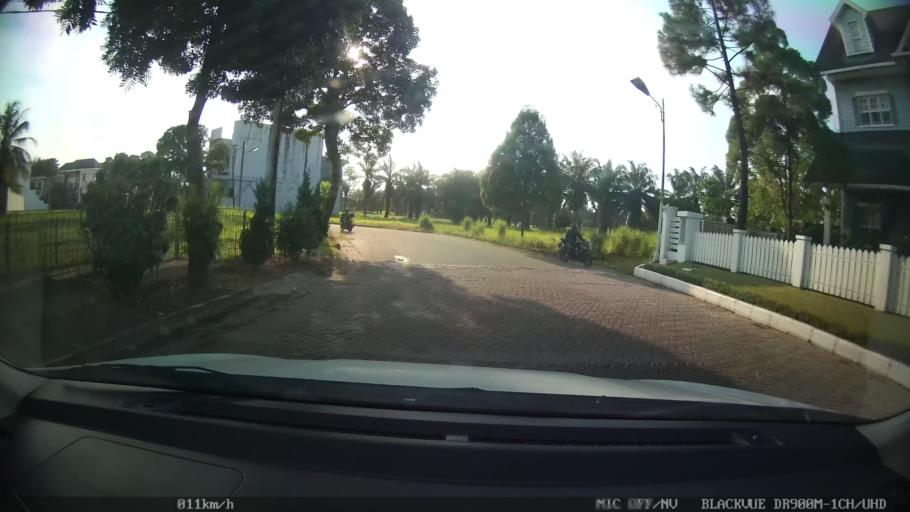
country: ID
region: North Sumatra
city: Medan
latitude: 3.6223
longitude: 98.6490
